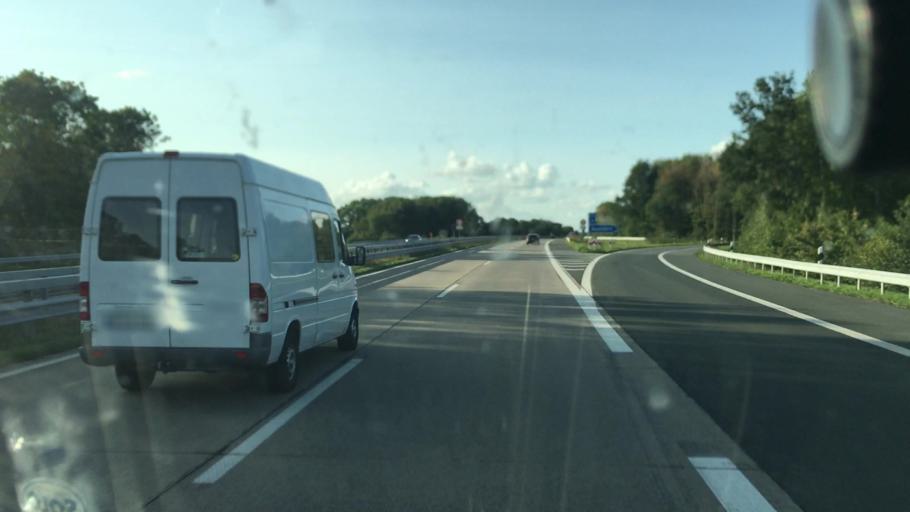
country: DE
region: Lower Saxony
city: Bockhorn
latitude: 53.4446
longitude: 8.0283
